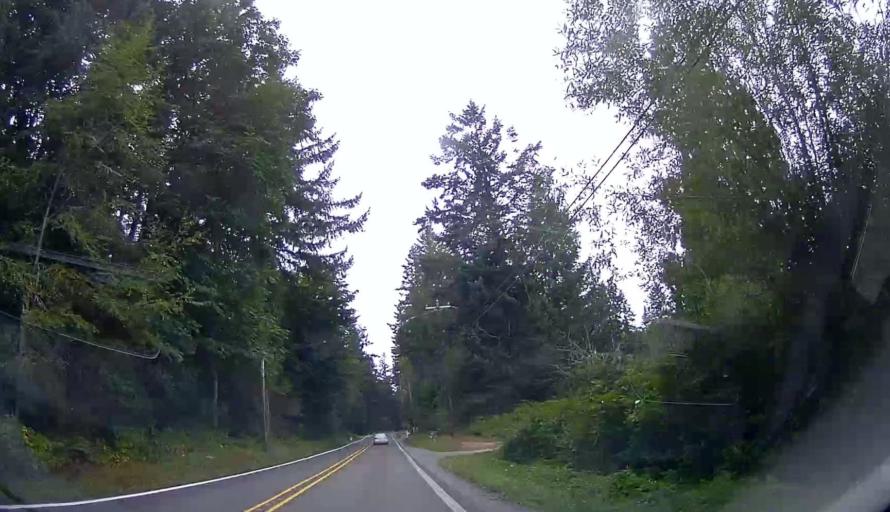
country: US
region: Washington
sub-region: Snohomish County
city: Warm Beach
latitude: 48.1105
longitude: -122.3417
